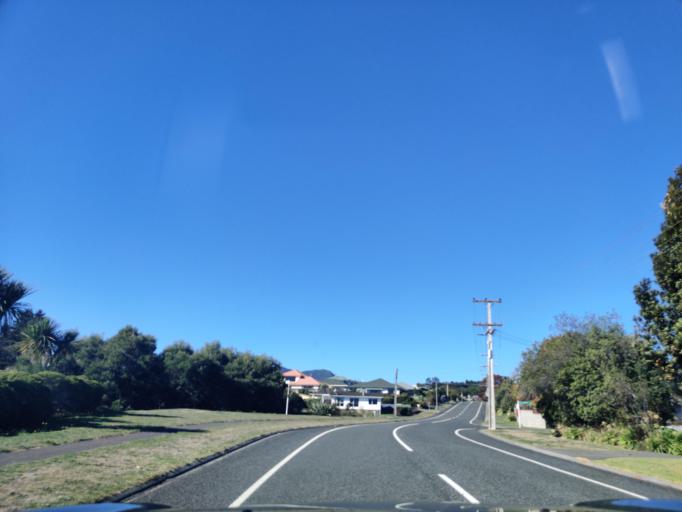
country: NZ
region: Waikato
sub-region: Taupo District
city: Taupo
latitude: -38.7083
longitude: 176.0916
